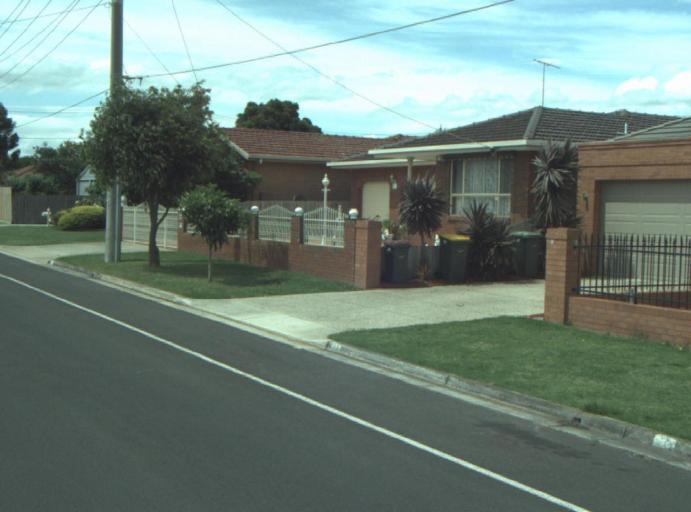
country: AU
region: Victoria
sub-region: Greater Geelong
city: Bell Park
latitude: -38.0910
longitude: 144.3415
